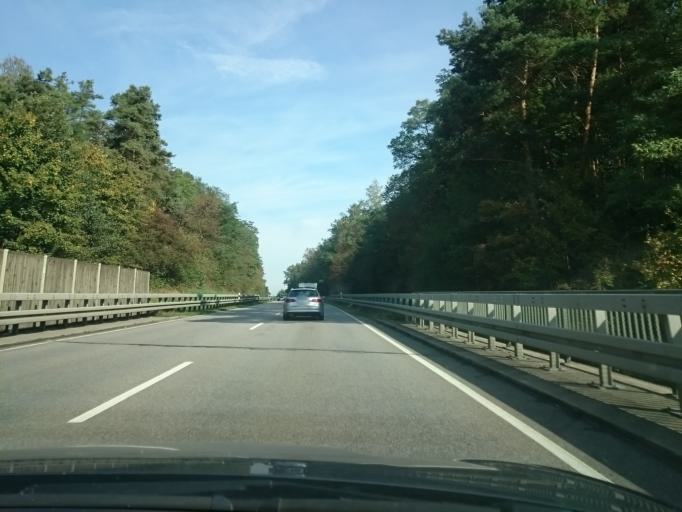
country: DE
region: Bavaria
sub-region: Upper Bavaria
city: Schrobenhausen
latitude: 48.5573
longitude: 11.2863
